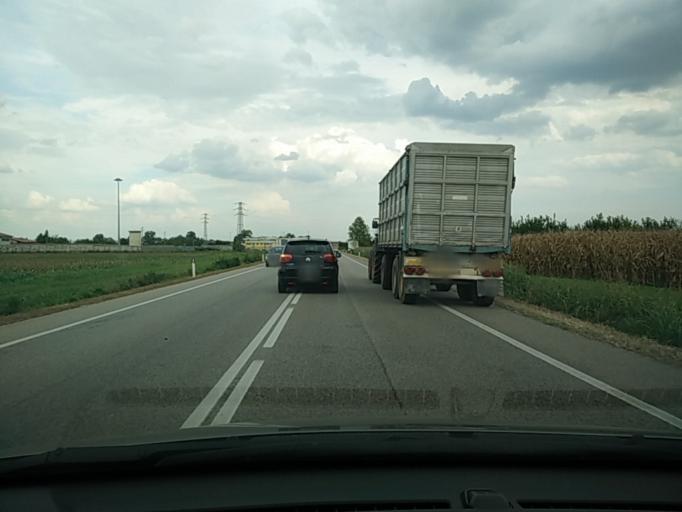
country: IT
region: Veneto
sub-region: Provincia di Treviso
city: Salvatronda
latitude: 45.6848
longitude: 11.9838
